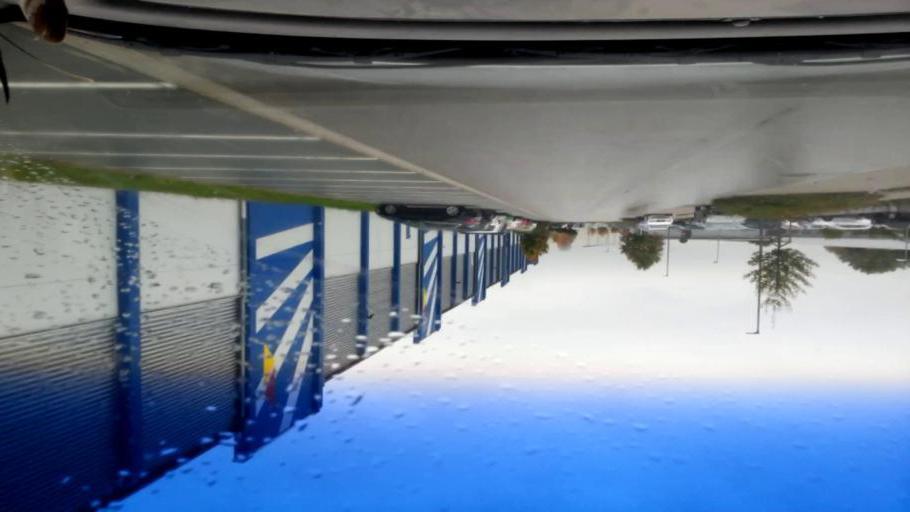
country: DE
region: Bavaria
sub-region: Upper Franconia
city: Schesslitz
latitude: 49.9804
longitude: 11.0497
